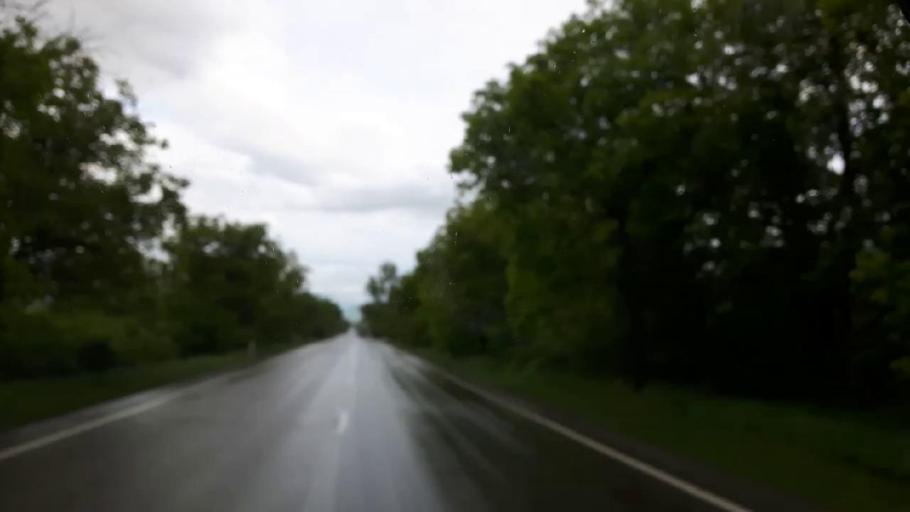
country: GE
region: Shida Kartli
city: Kaspi
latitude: 41.9693
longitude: 44.4570
